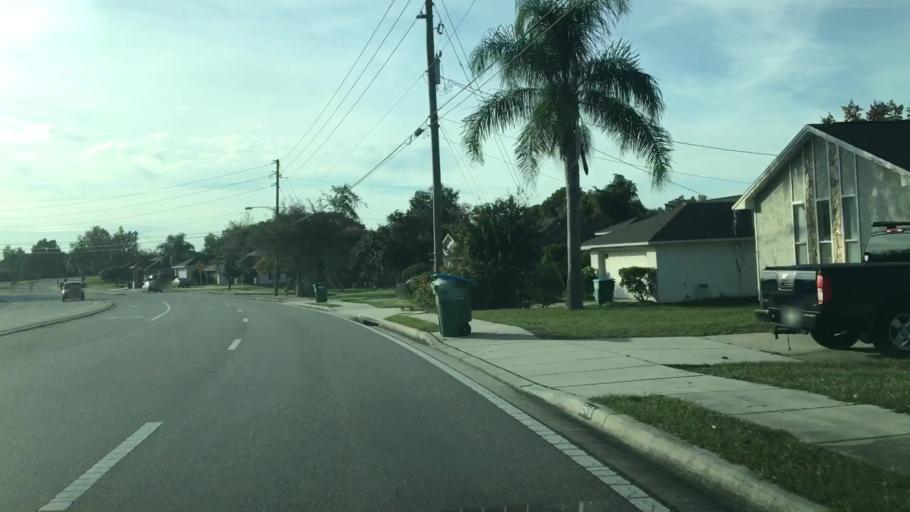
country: US
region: Florida
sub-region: Volusia County
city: Deltona
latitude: 28.9179
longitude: -81.2574
